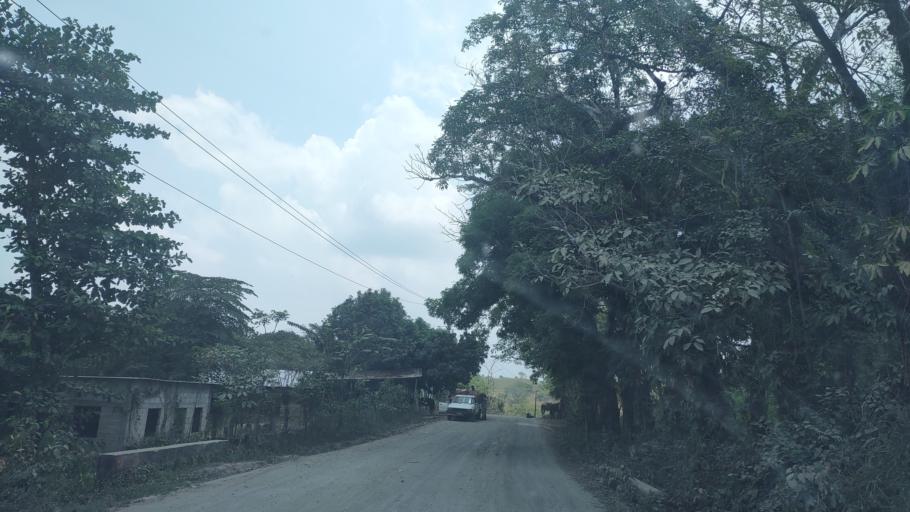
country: MX
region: Tabasco
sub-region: Huimanguillo
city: Francisco Rueda
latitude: 17.6476
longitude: -93.9062
